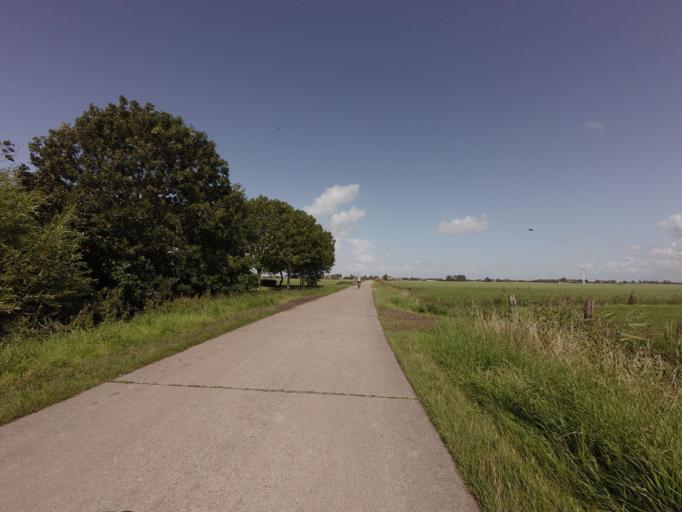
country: NL
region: Friesland
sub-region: Sudwest Fryslan
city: Makkum
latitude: 53.0698
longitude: 5.4543
